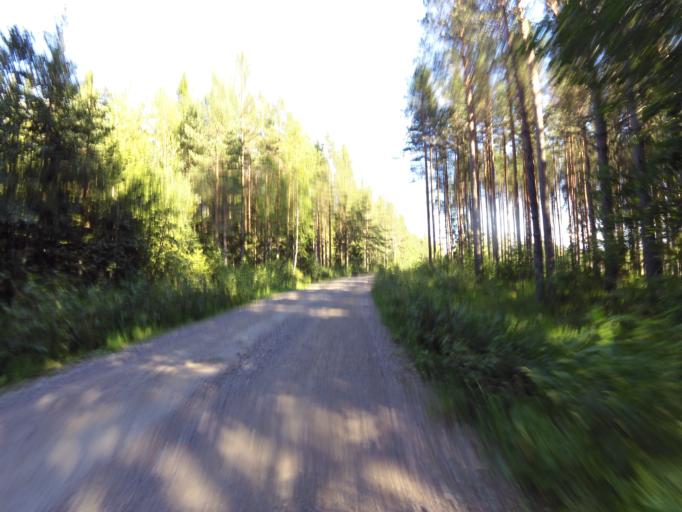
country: SE
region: Gaevleborg
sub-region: Hofors Kommun
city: Hofors
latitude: 60.6442
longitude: 16.2787
